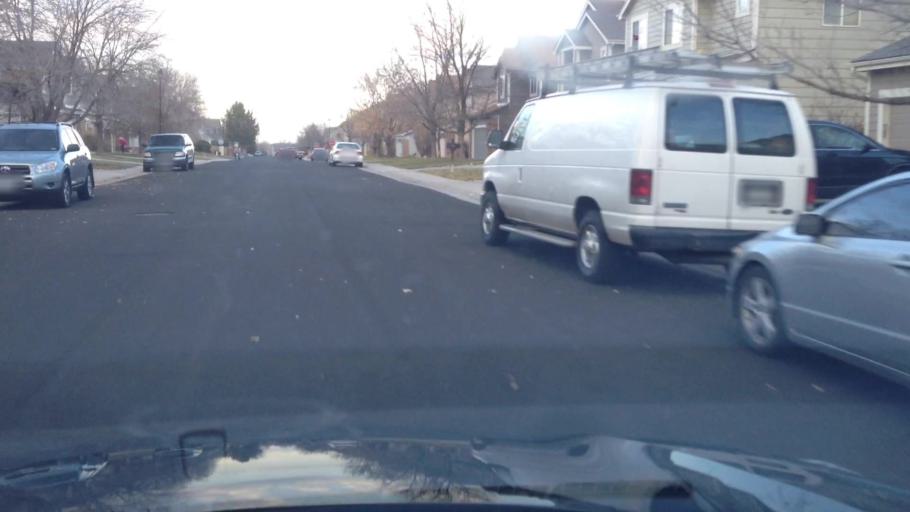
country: US
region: Colorado
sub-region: Douglas County
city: Stonegate
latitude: 39.5166
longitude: -104.7908
